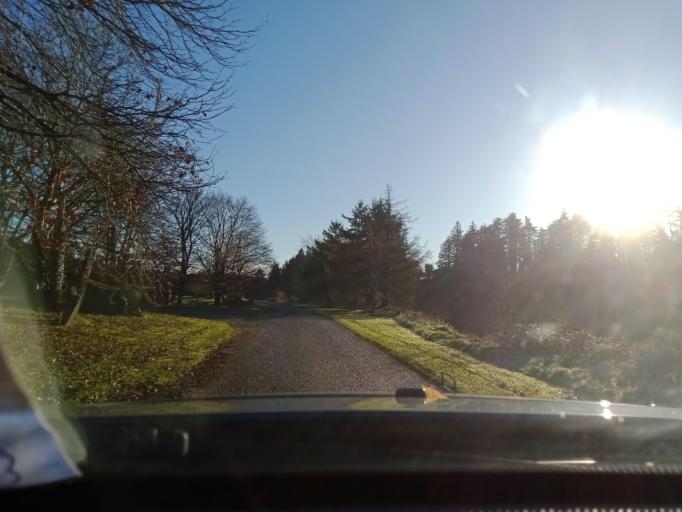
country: IE
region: Munster
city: Carrick-on-Suir
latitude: 52.4262
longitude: -7.3892
